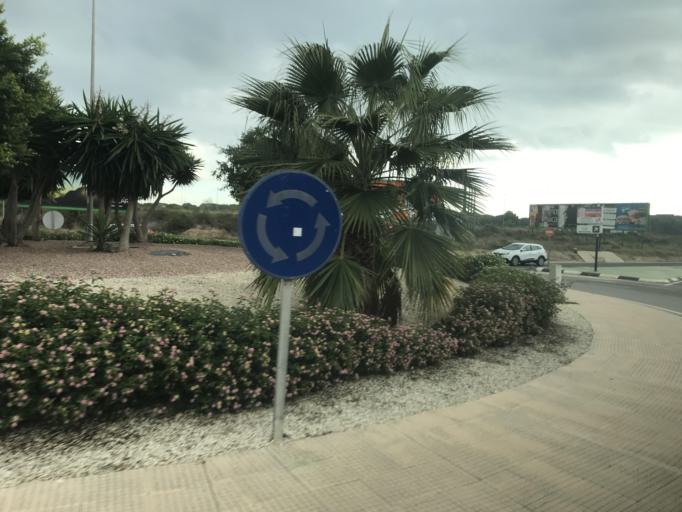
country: ES
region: Valencia
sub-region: Provincia de Alicante
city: Guardamar del Segura
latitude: 38.1194
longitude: -0.6569
